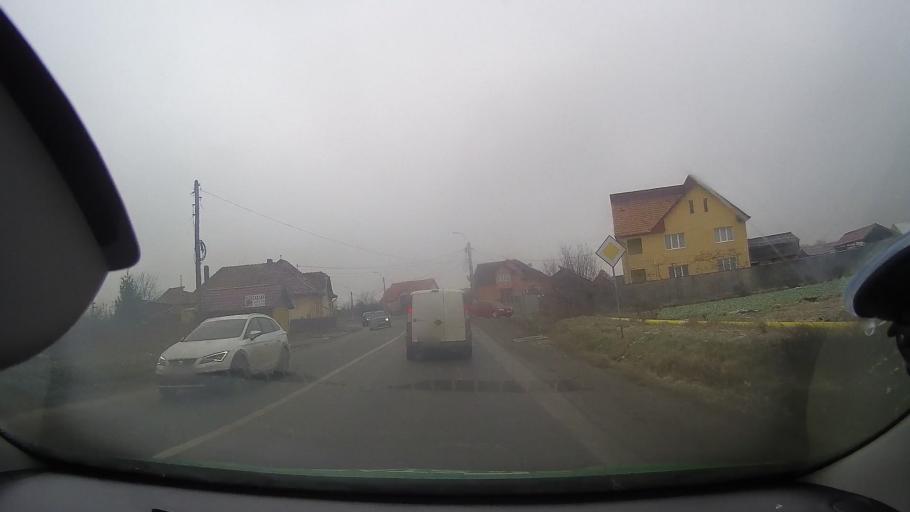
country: RO
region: Cluj
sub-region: Comuna Mihai Viteazu
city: Mihai Viteazu
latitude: 46.5423
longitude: 23.7713
